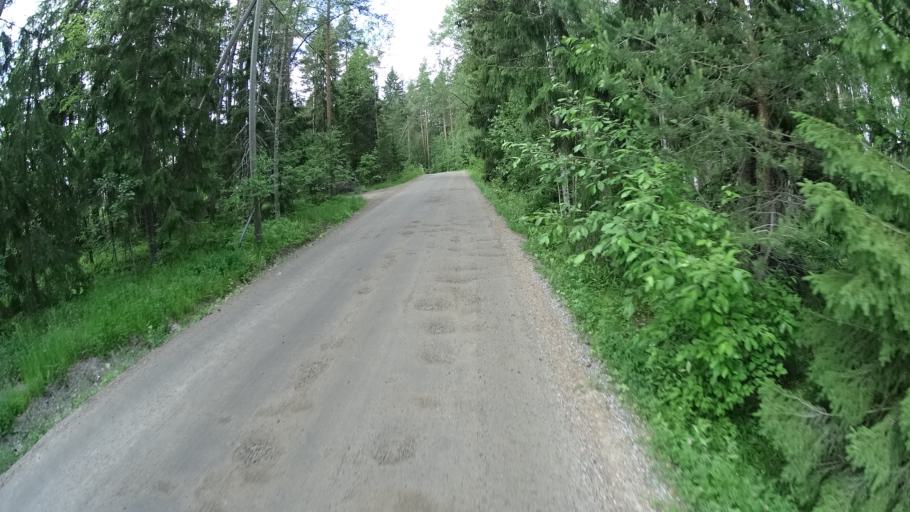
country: FI
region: Uusimaa
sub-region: Helsinki
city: Sibbo
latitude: 60.2831
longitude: 25.3152
